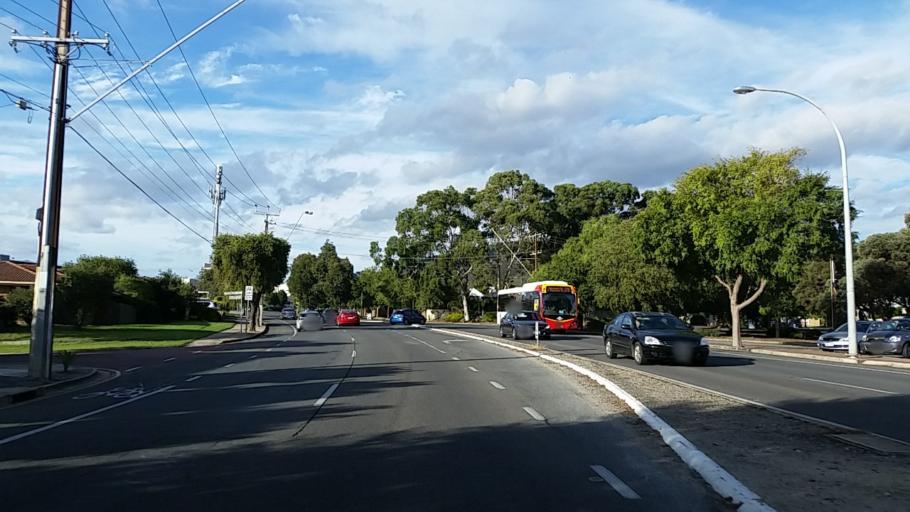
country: AU
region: South Australia
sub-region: Campbelltown
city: Athelstone
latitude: -34.8877
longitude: 138.6885
